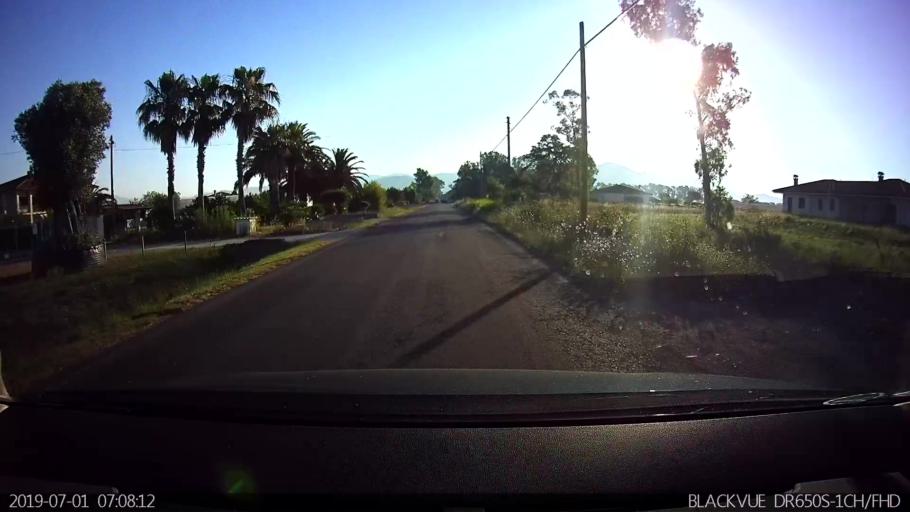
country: IT
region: Latium
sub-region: Provincia di Latina
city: Borgo Hermada
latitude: 41.2953
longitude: 13.1474
